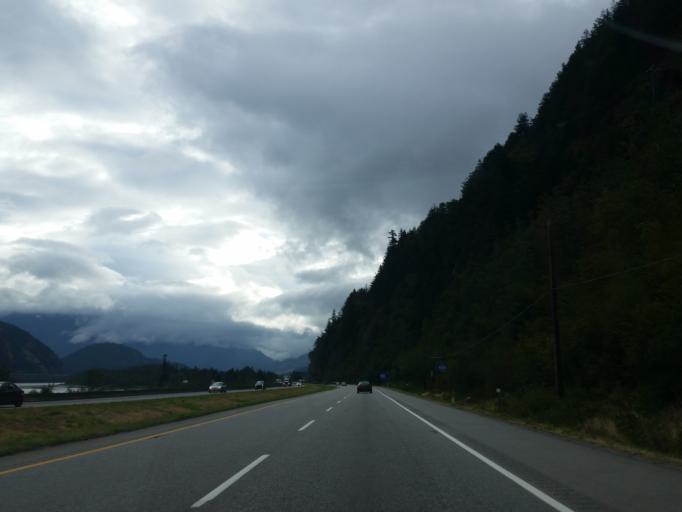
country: CA
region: British Columbia
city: Hope
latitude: 49.3638
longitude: -121.5386
